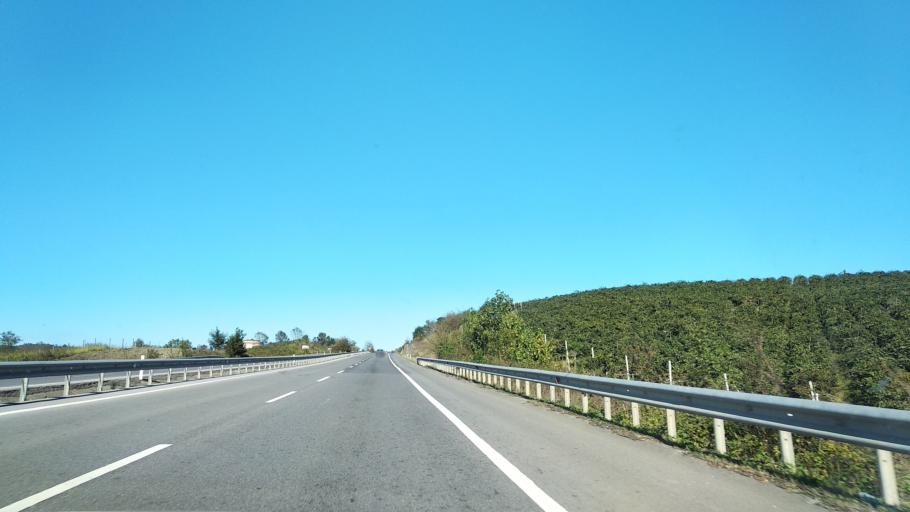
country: TR
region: Sakarya
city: Ortakoy
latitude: 41.0429
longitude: 30.6235
